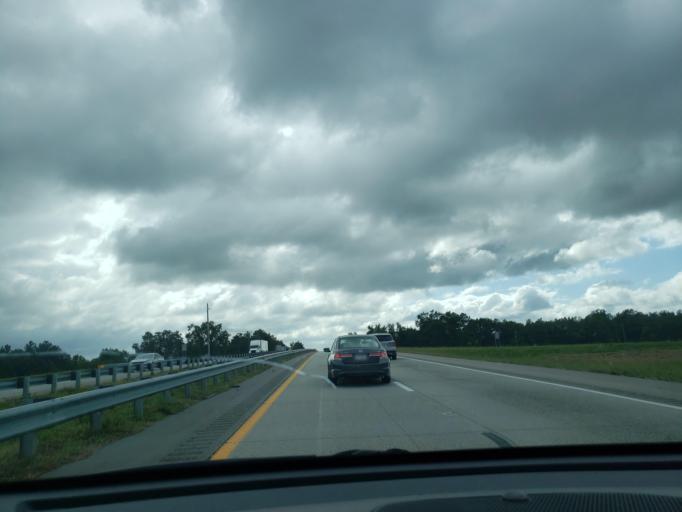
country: US
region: North Carolina
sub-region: Vance County
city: Henderson
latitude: 36.3947
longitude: -78.3373
